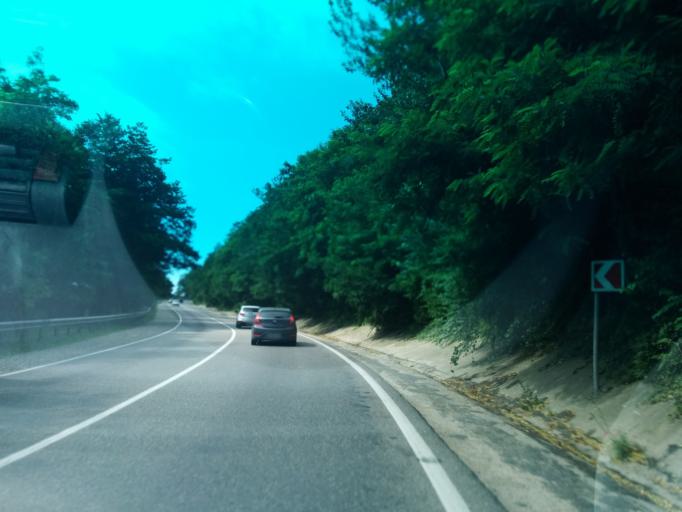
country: RU
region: Krasnodarskiy
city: Nebug
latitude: 44.1764
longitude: 38.9735
